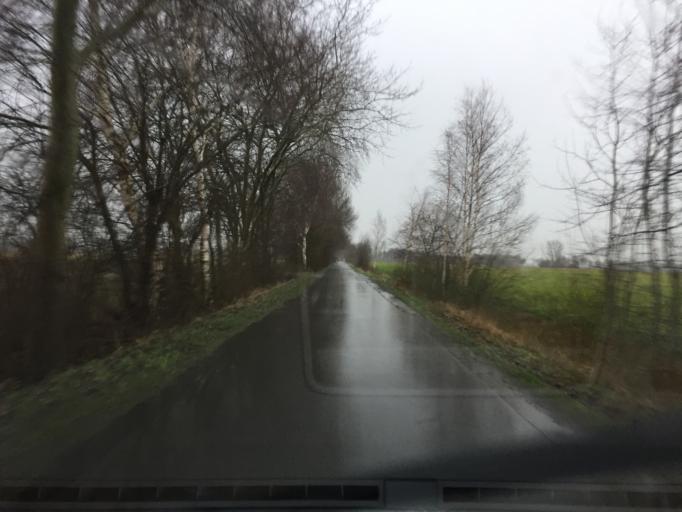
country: DE
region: Lower Saxony
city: Sulingen
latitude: 52.6509
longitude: 8.8340
